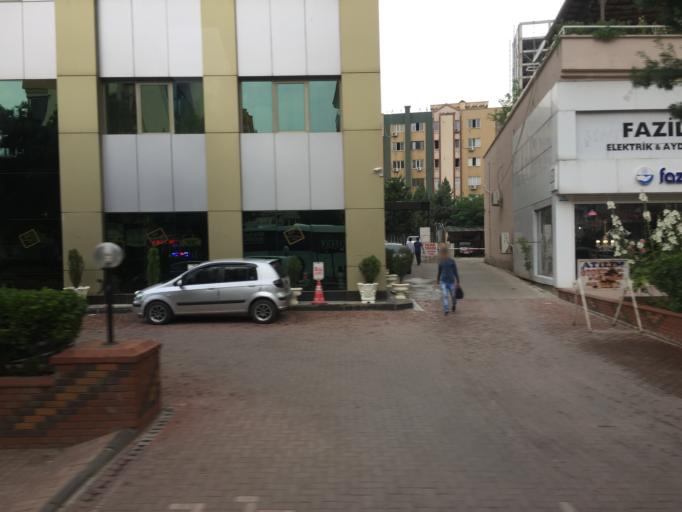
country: TR
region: Gaziantep
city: Gaziantep
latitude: 37.0717
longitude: 37.3721
